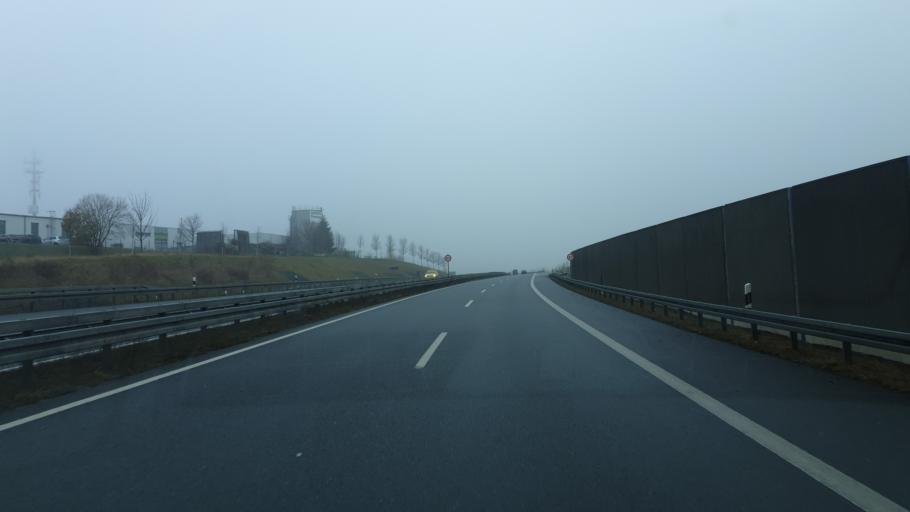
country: DE
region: Saxony
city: Gornau
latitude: 50.7866
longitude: 12.9958
